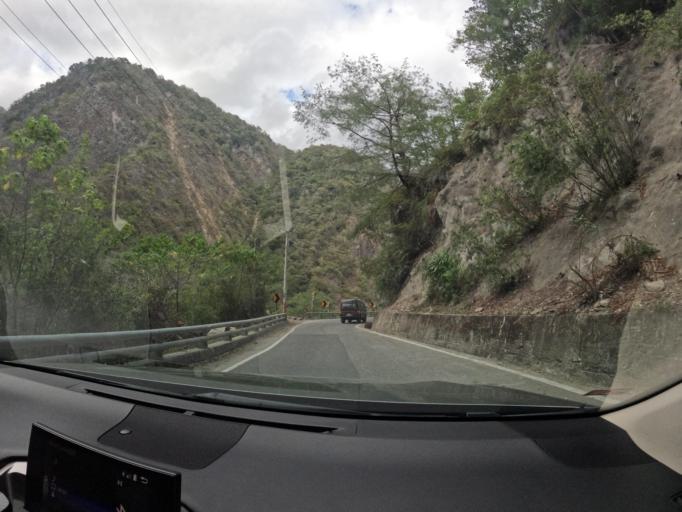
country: TW
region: Taiwan
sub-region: Taitung
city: Taitung
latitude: 23.1353
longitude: 121.1152
